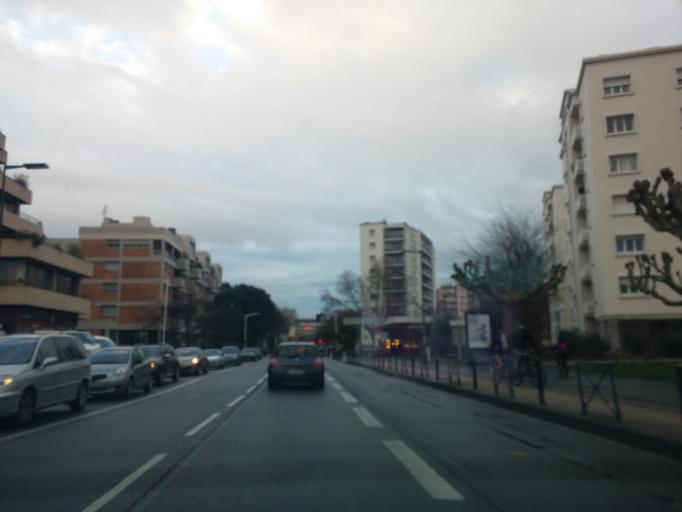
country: FR
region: Midi-Pyrenees
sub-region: Departement de la Haute-Garonne
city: Toulouse
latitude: 43.5840
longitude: 1.4400
